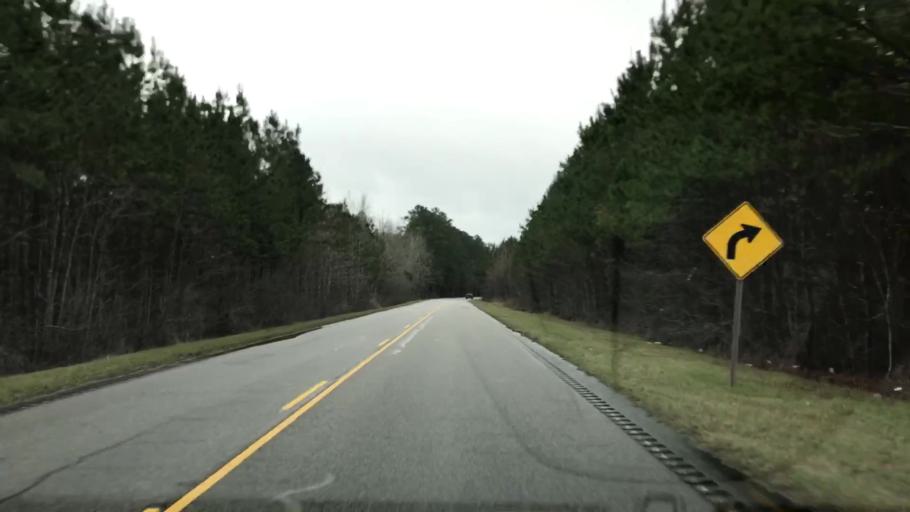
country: US
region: South Carolina
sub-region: Williamsburg County
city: Andrews
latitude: 33.5633
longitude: -79.4539
